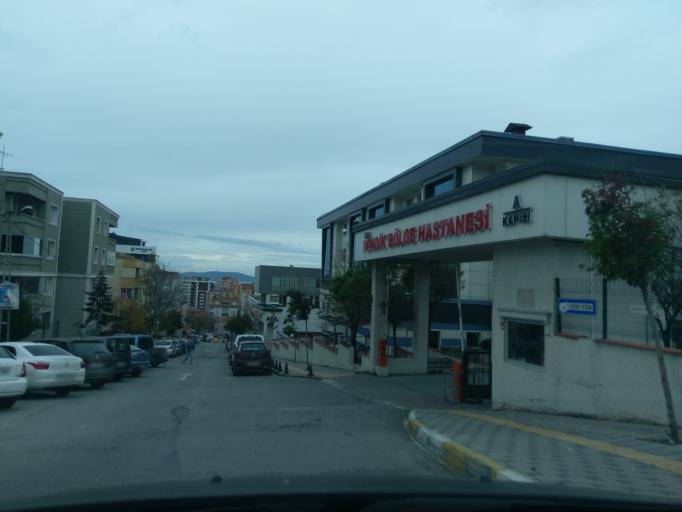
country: TR
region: Istanbul
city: Pendik
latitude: 40.8826
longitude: 29.2464
